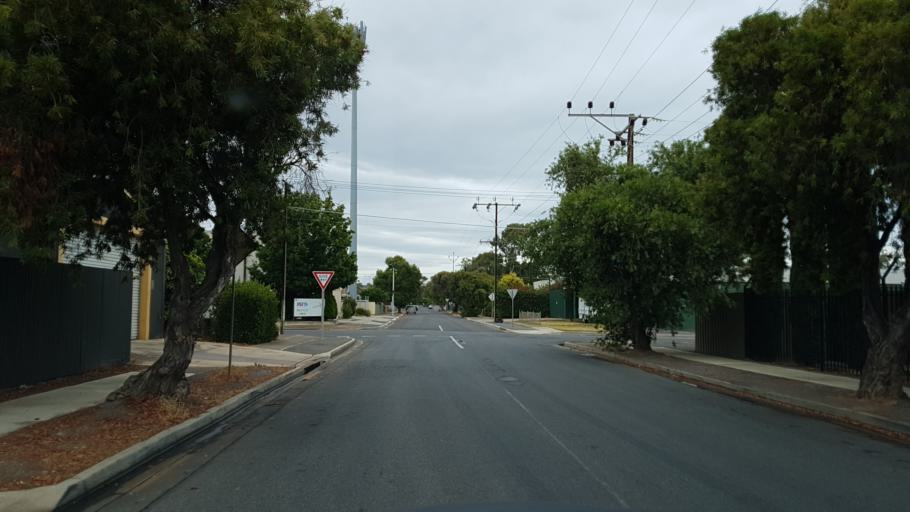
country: AU
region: South Australia
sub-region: Holdfast Bay
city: North Brighton
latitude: -34.9976
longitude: 138.5264
